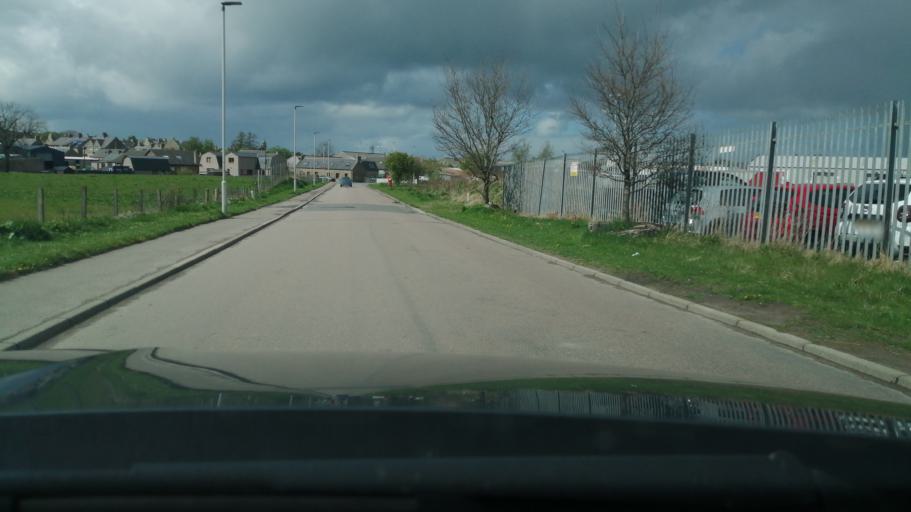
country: GB
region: Scotland
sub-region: Moray
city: Keith
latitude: 57.5368
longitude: -2.9434
